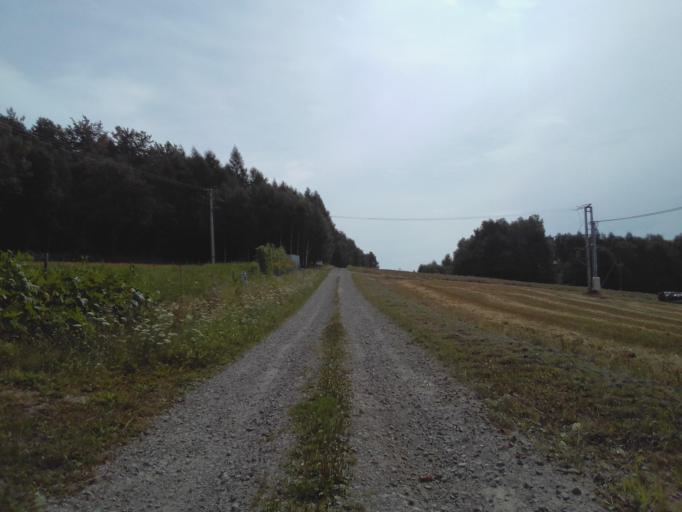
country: PL
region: Subcarpathian Voivodeship
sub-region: Powiat strzyzowski
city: Frysztak
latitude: 49.8664
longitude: 21.5723
